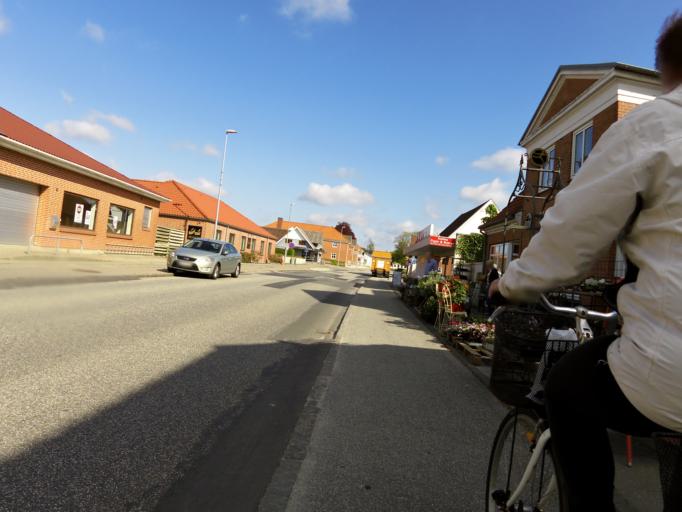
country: DK
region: South Denmark
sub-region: Vejen Kommune
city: Rodding
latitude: 55.3679
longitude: 9.0606
